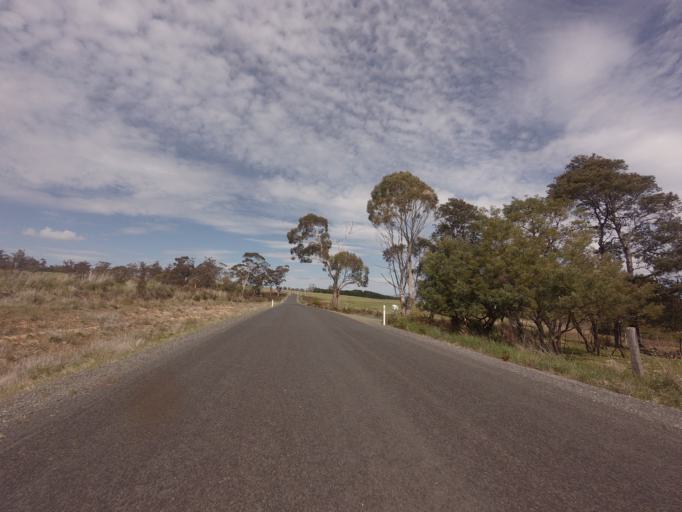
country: AU
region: Tasmania
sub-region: Northern Midlands
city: Longford
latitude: -41.7633
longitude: 147.2103
